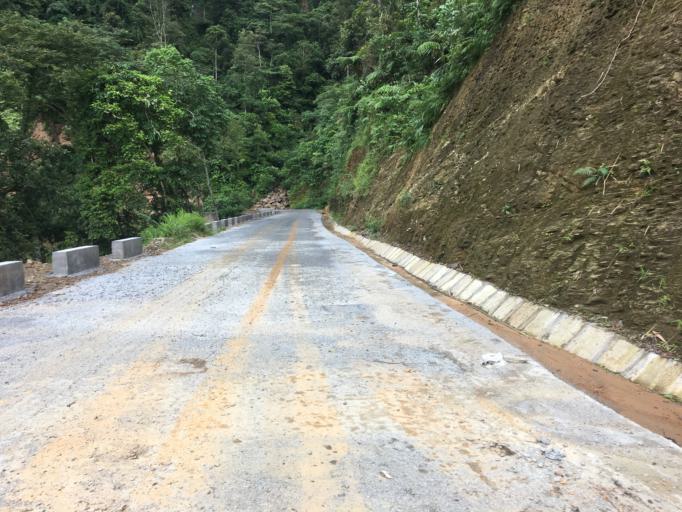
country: VN
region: Ha Giang
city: Thi Tran Tam Son
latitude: 22.9812
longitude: 105.0590
